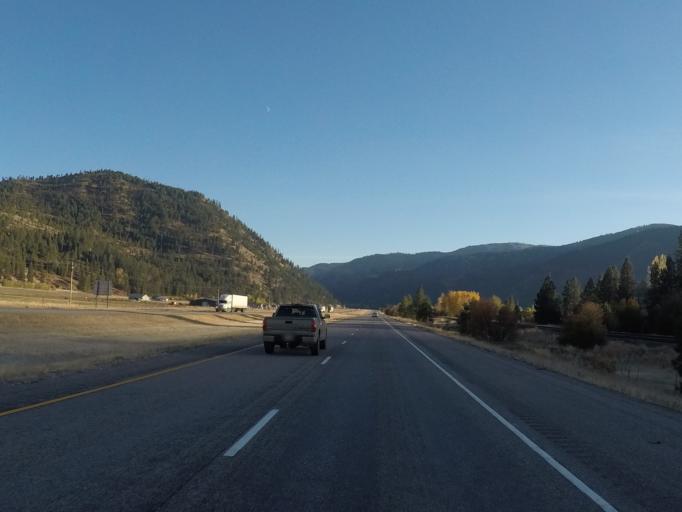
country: US
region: Montana
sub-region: Missoula County
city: Clinton
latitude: 46.7650
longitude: -113.7103
